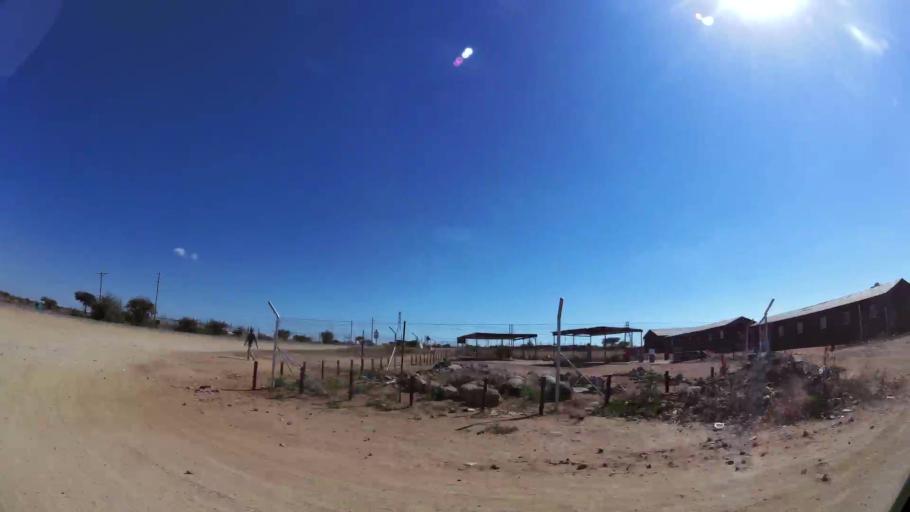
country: ZA
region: Limpopo
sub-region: Capricorn District Municipality
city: Polokwane
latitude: -23.8926
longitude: 29.4098
